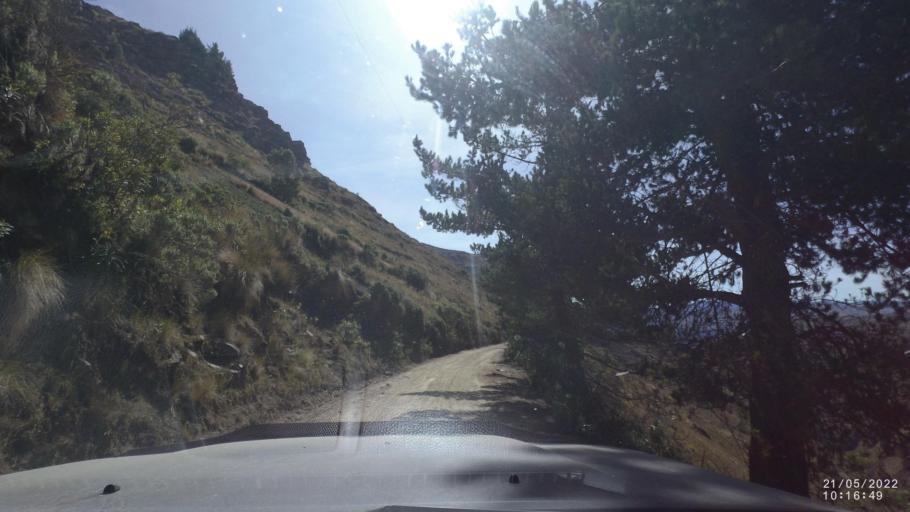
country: BO
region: Cochabamba
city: Colomi
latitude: -17.3313
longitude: -65.9661
